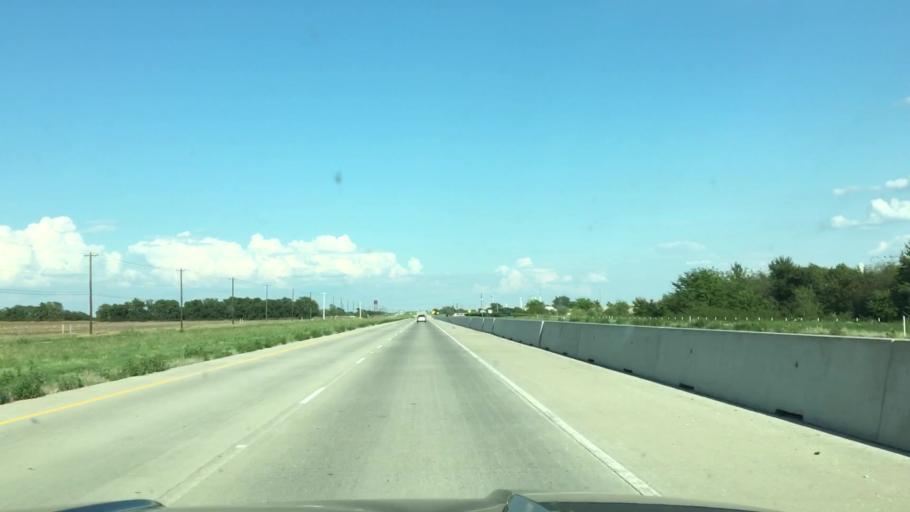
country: US
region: Texas
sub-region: Tarrant County
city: Haslet
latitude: 33.0353
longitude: -97.3584
